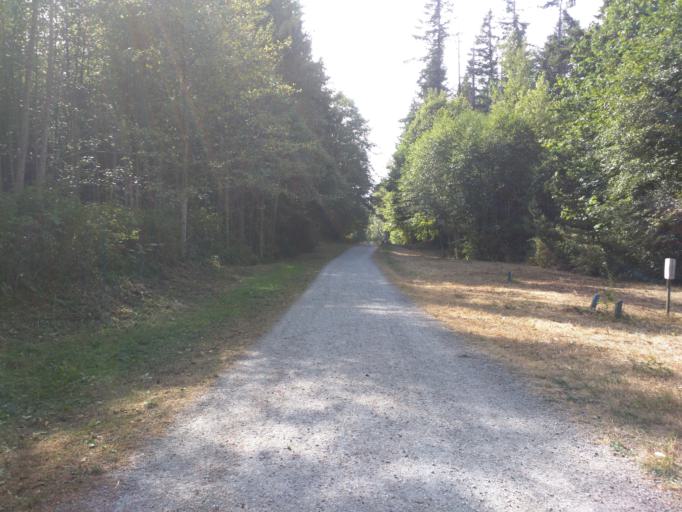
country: US
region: Washington
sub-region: Whatcom County
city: Geneva
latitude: 48.7522
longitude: -122.4351
